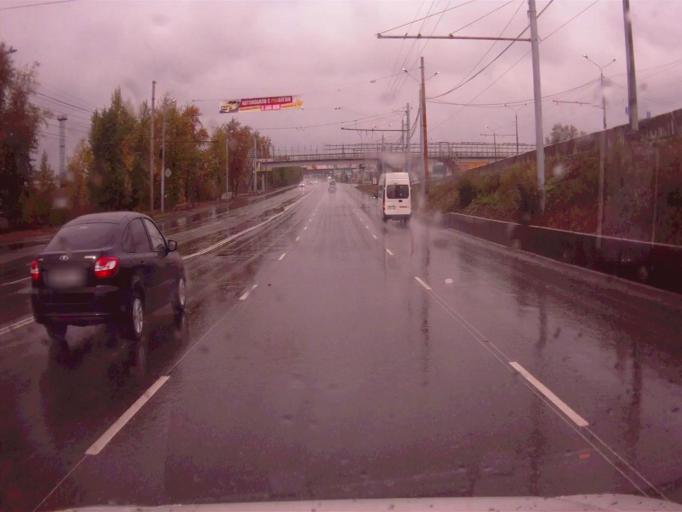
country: RU
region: Chelyabinsk
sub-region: Gorod Chelyabinsk
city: Chelyabinsk
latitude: 55.1995
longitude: 61.3859
